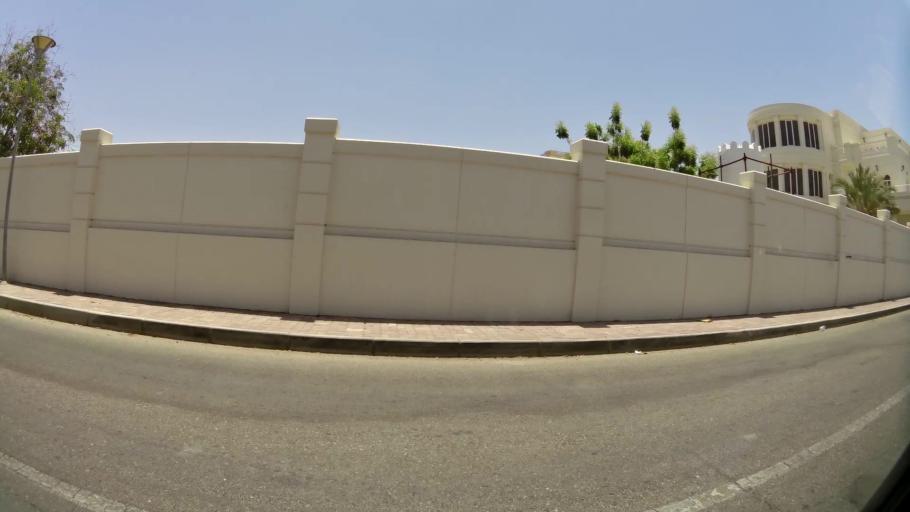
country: OM
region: Muhafazat Masqat
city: Bawshar
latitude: 23.6104
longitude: 58.4659
